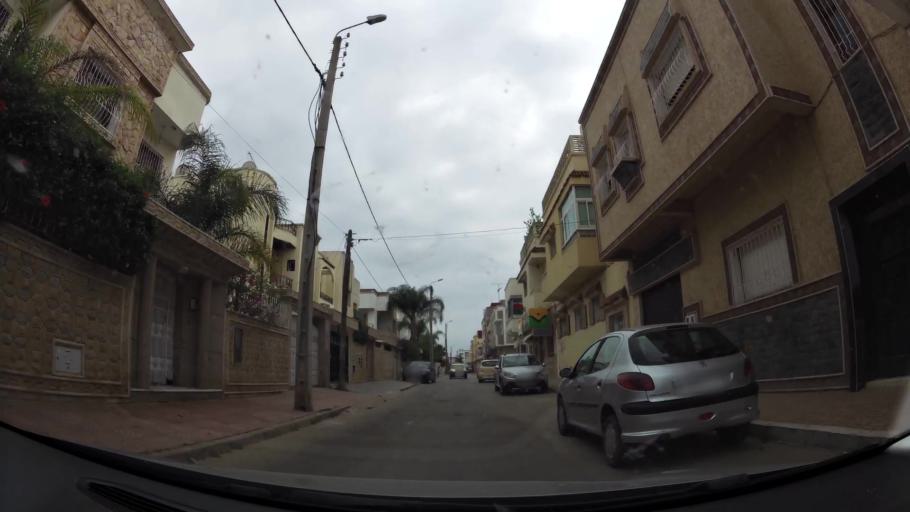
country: MA
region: Rabat-Sale-Zemmour-Zaer
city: Sale
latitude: 34.0309
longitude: -6.7976
